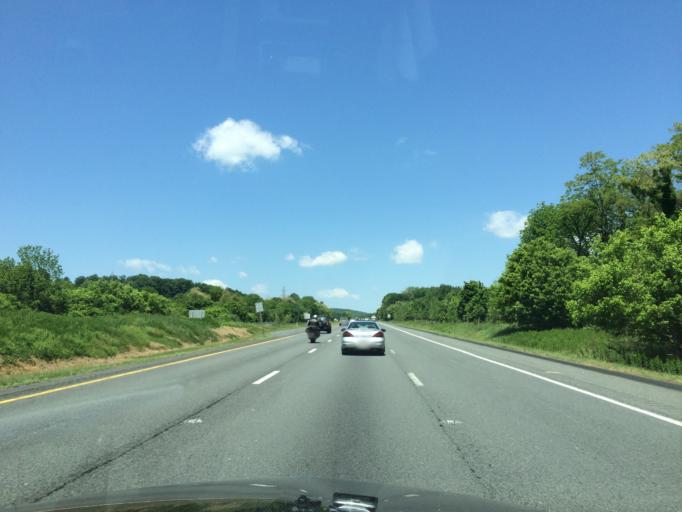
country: US
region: Maryland
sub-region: Frederick County
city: Myersville
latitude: 39.5003
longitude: -77.5737
